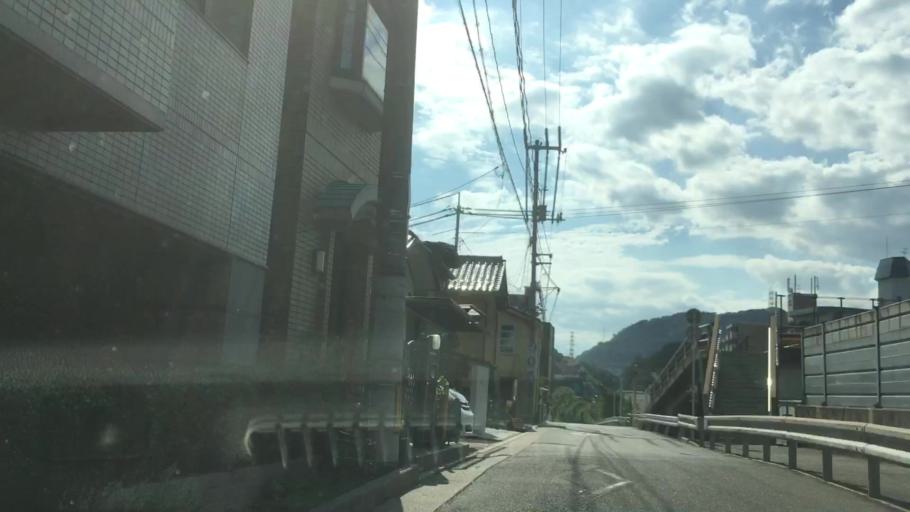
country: JP
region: Hiroshima
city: Hiroshima-shi
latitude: 34.3916
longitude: 132.4107
